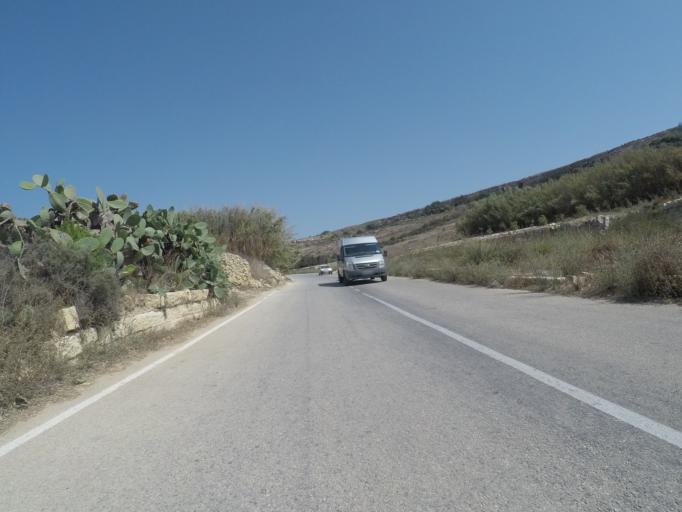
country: MT
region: L-Imgarr
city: Imgarr
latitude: 35.9191
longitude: 14.3504
